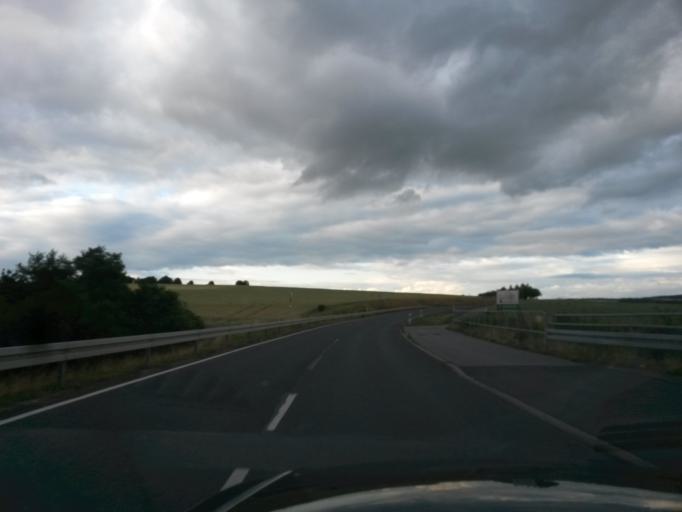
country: DE
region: Bavaria
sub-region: Regierungsbezirk Unterfranken
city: Estenfeld
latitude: 49.8184
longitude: 9.9865
